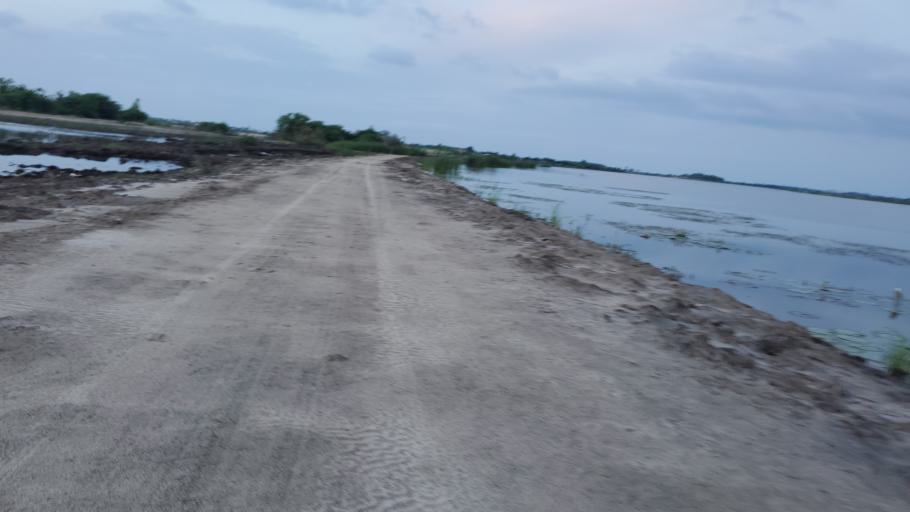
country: SN
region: Saint-Louis
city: Saint-Louis
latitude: 16.0416
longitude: -16.4167
